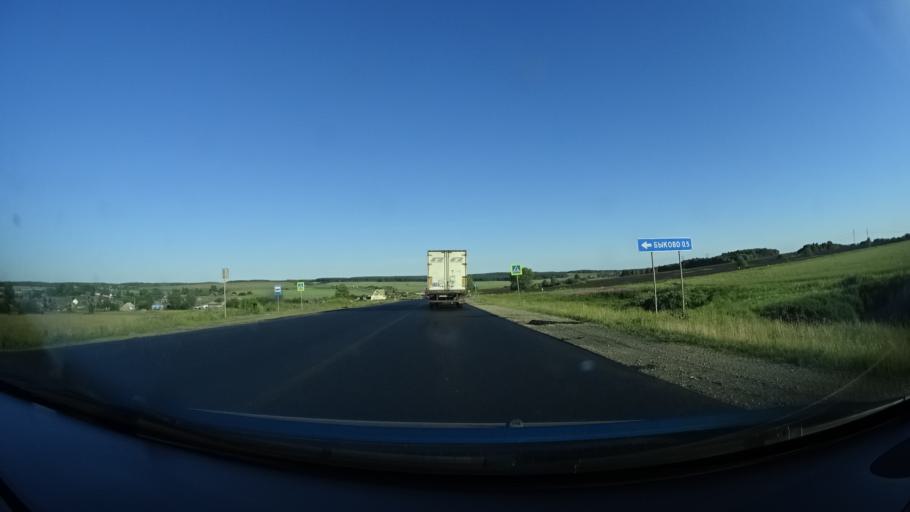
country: RU
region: Sverdlovsk
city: Achit
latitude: 56.8963
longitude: 57.6026
